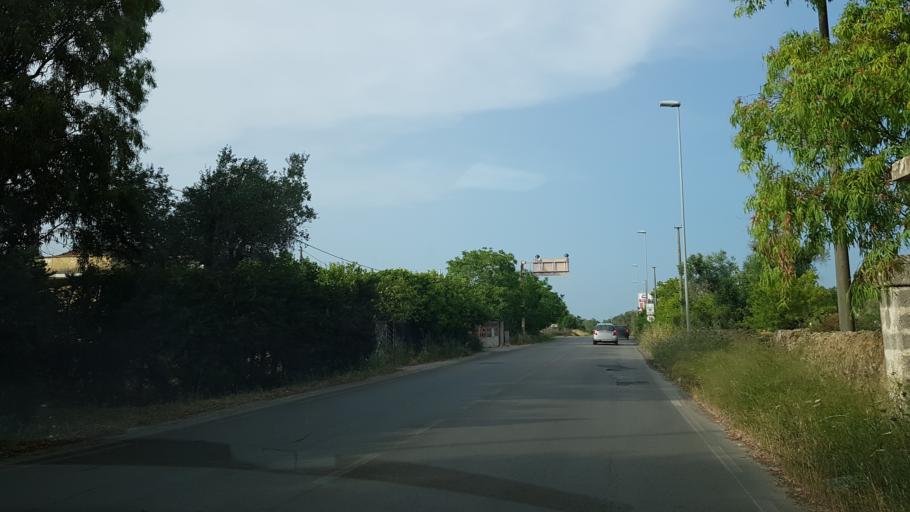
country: IT
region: Apulia
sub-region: Provincia di Brindisi
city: Cellino San Marco
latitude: 40.4783
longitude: 17.9796
